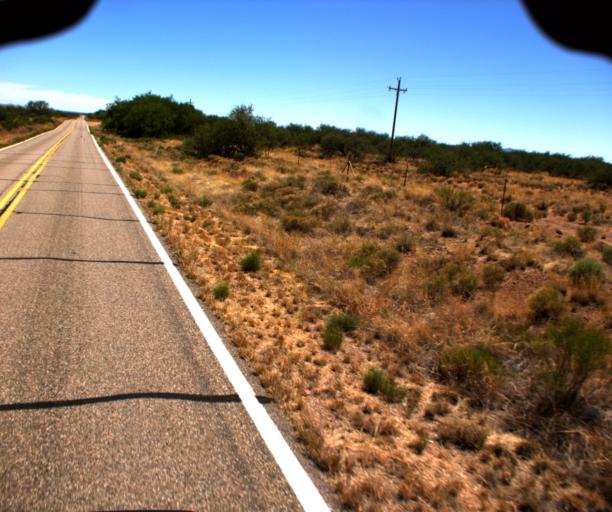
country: US
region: Arizona
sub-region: Pima County
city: Three Points
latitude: 31.7267
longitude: -111.4880
